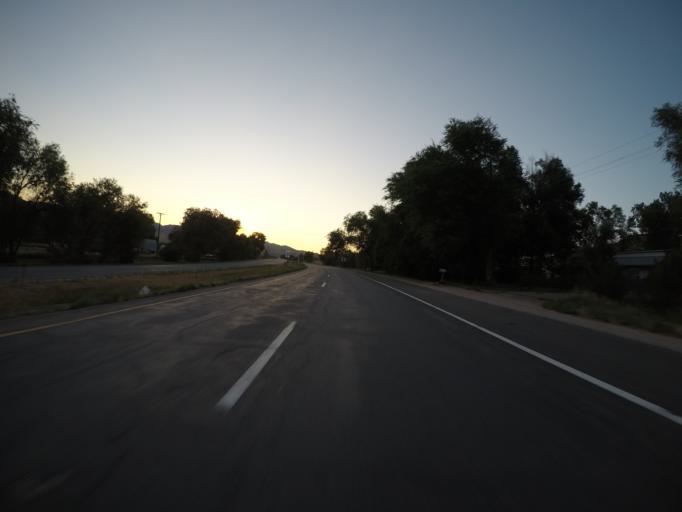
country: US
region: Colorado
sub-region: Larimer County
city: Laporte
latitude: 40.6602
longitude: -105.1837
